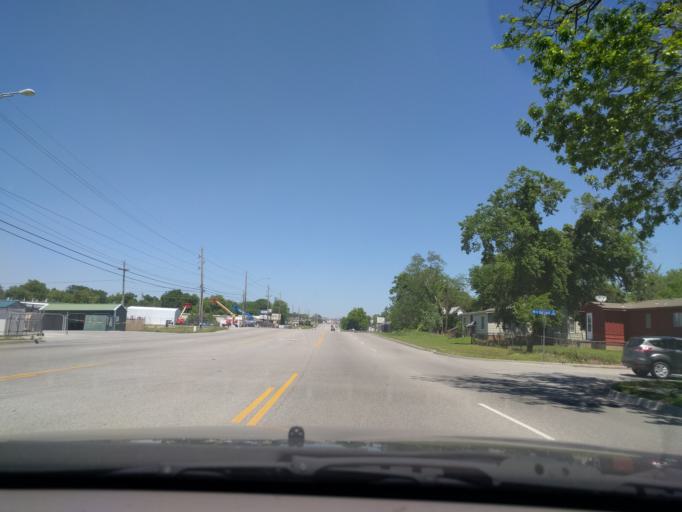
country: US
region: Oklahoma
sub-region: Tulsa County
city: Broken Arrow
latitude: 36.0542
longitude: -95.7974
